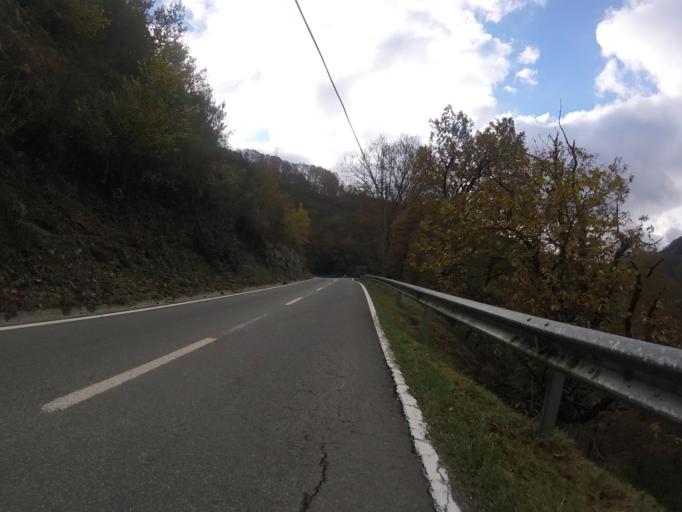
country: ES
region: Navarre
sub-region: Provincia de Navarra
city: Goizueta
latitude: 43.2104
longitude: -1.8568
